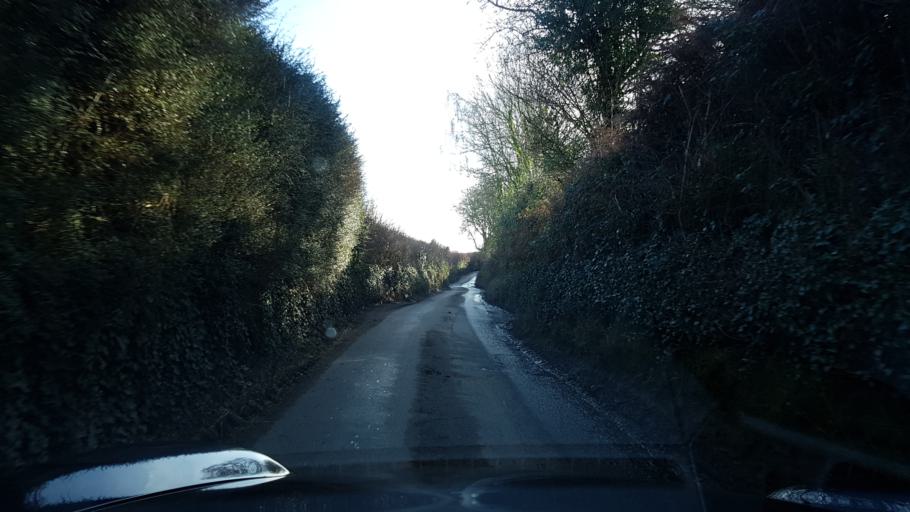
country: GB
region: England
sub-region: Dorset
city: Bridport
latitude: 50.7566
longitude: -2.7748
